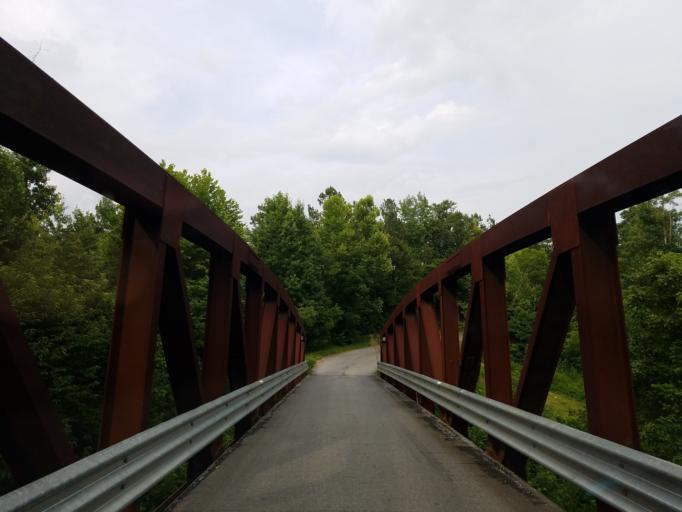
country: US
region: Georgia
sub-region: Bartow County
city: Rydal
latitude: 34.3904
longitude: -84.6691
